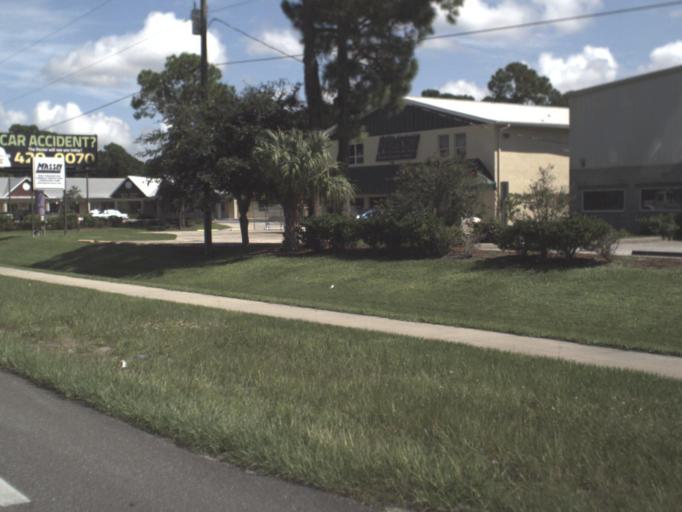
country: US
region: Florida
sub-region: Sarasota County
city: North Port
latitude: 27.0195
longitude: -82.1637
